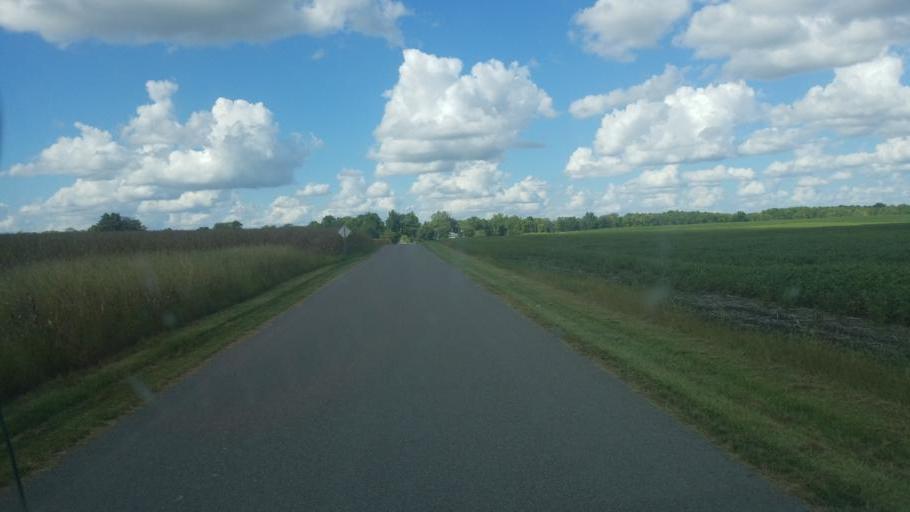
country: US
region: Ohio
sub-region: Hardin County
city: Kenton
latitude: 40.5328
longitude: -83.5424
